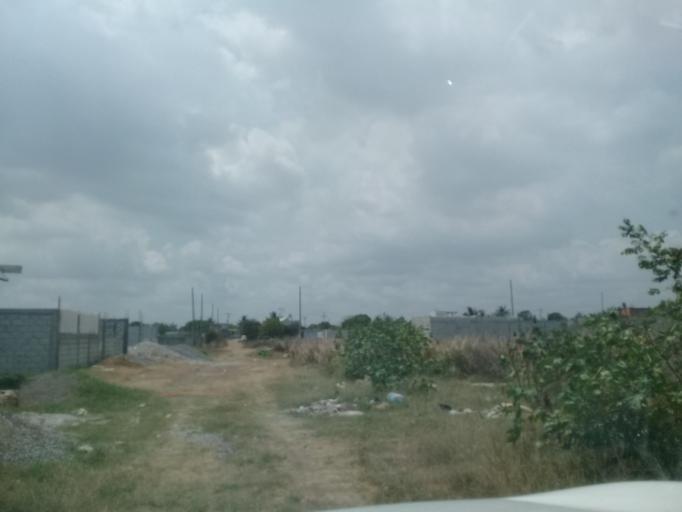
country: MX
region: Veracruz
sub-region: Veracruz
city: Las Amapolas
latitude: 19.1419
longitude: -96.2347
